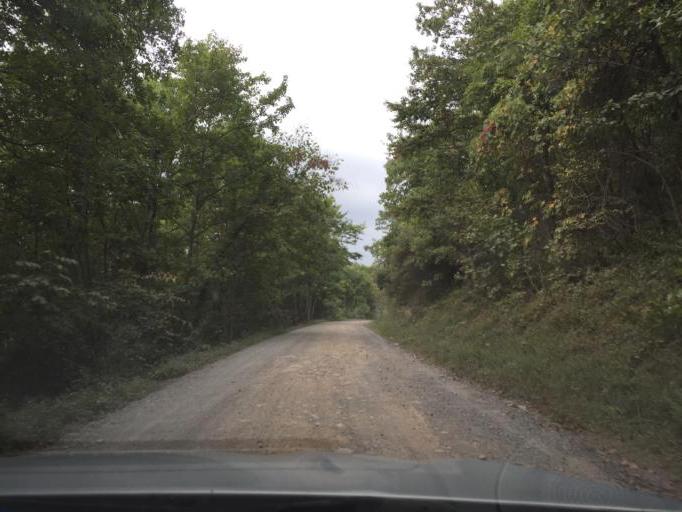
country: US
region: Virginia
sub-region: Shenandoah County
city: Woodstock
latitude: 38.8735
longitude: -78.4439
